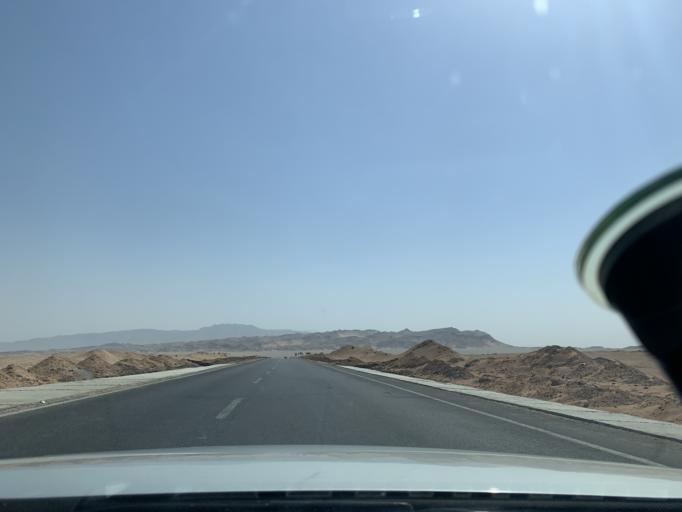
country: EG
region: As Suways
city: Ain Sukhna
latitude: 29.0788
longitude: 32.6275
